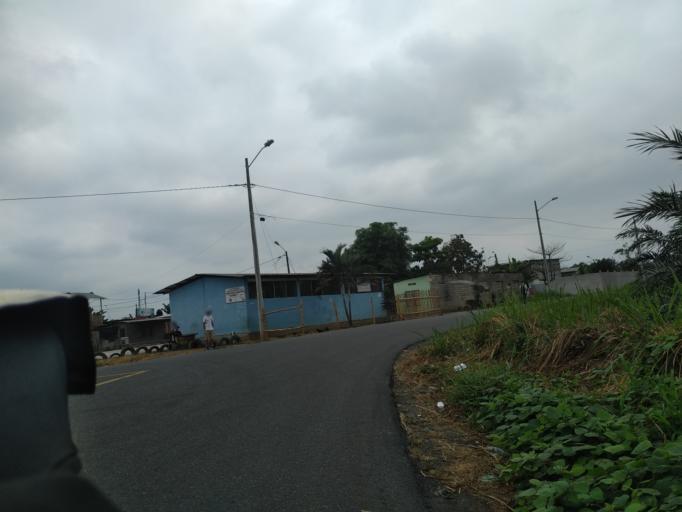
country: EC
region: Los Rios
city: Quevedo
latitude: -1.0233
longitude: -79.4372
